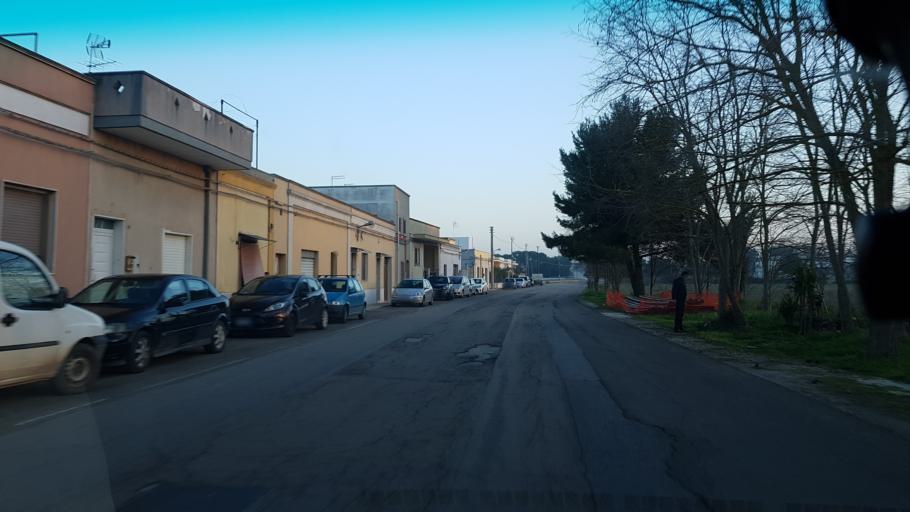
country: IT
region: Apulia
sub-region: Provincia di Brindisi
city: Mesagne
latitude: 40.5696
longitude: 17.8038
